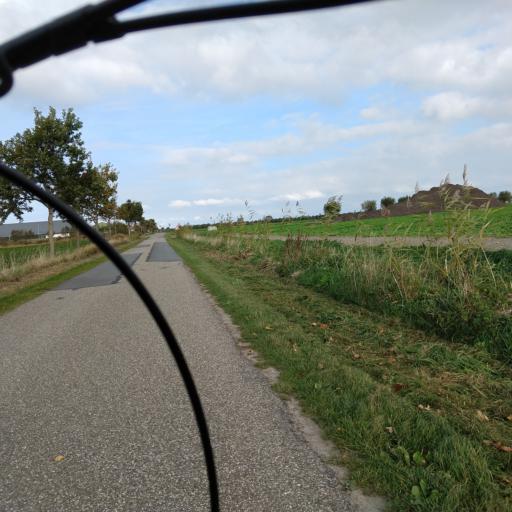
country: NL
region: Zeeland
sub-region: Schouwen-Duiveland
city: Scharendijke
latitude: 51.7081
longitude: 3.9326
